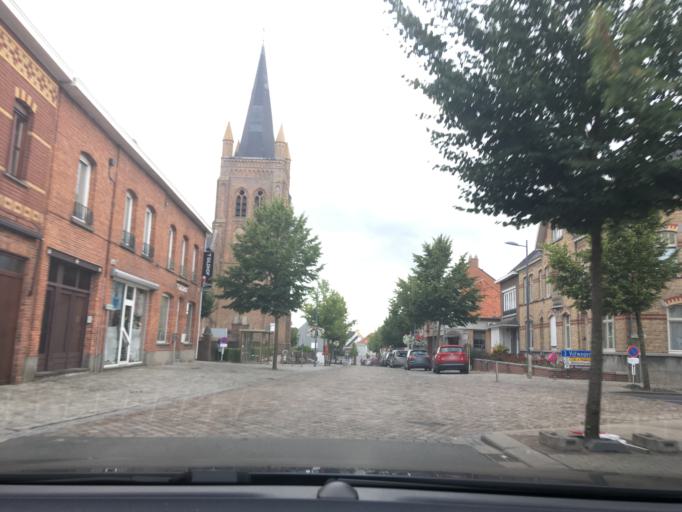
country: BE
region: Flanders
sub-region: Provincie West-Vlaanderen
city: Staden
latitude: 50.9321
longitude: 3.0123
